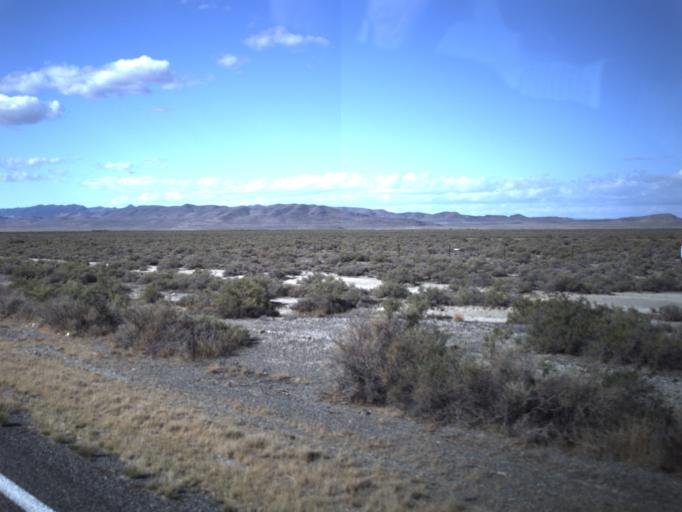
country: US
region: Utah
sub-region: Millard County
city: Delta
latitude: 39.1251
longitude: -112.7352
